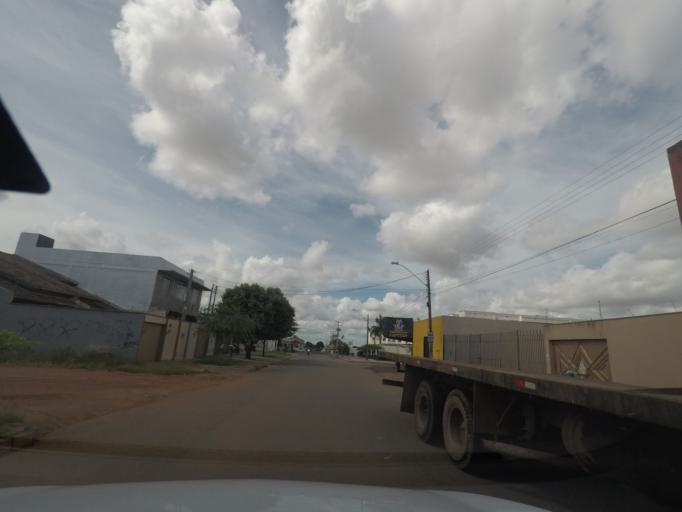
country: BR
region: Goias
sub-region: Goiania
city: Goiania
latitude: -16.7426
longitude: -49.3433
